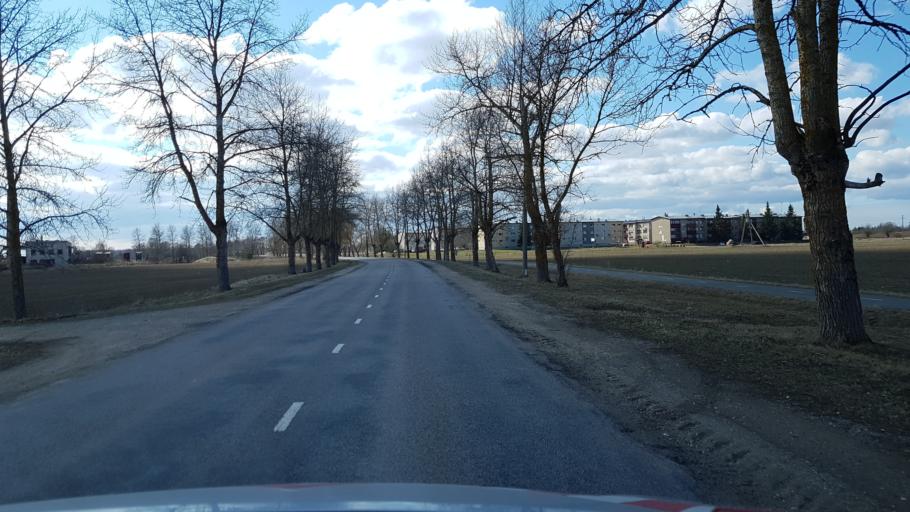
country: EE
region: Laeaene-Virumaa
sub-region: Rakvere linn
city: Rakvere
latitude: 59.3312
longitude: 26.2968
